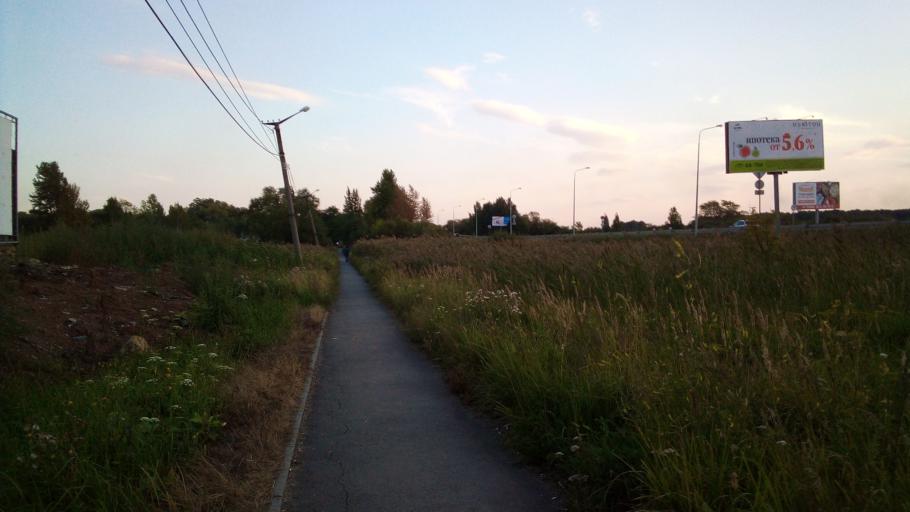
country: RU
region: Chelyabinsk
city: Potanino
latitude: 55.2943
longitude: 61.5122
